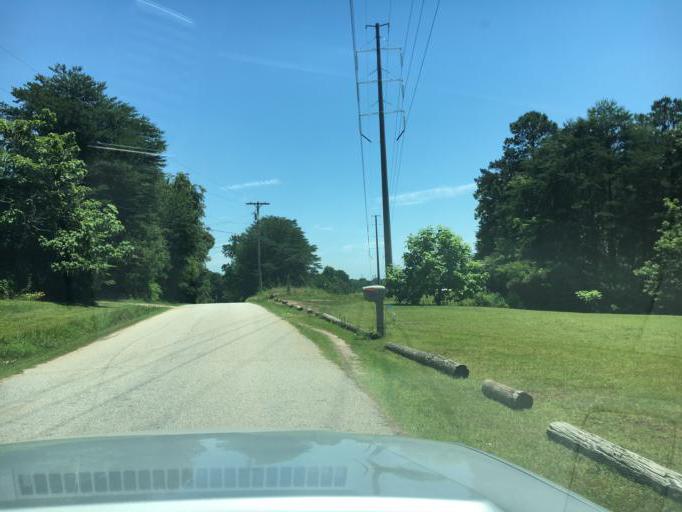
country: US
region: South Carolina
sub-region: Greenville County
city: Greer
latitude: 34.9606
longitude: -82.2207
